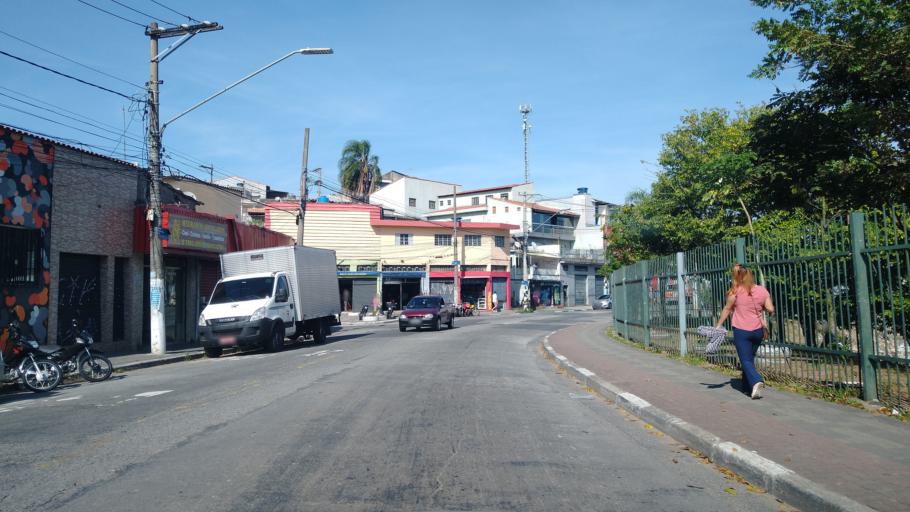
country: BR
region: Sao Paulo
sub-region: Sao Paulo
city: Sao Paulo
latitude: -23.4647
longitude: -46.6679
